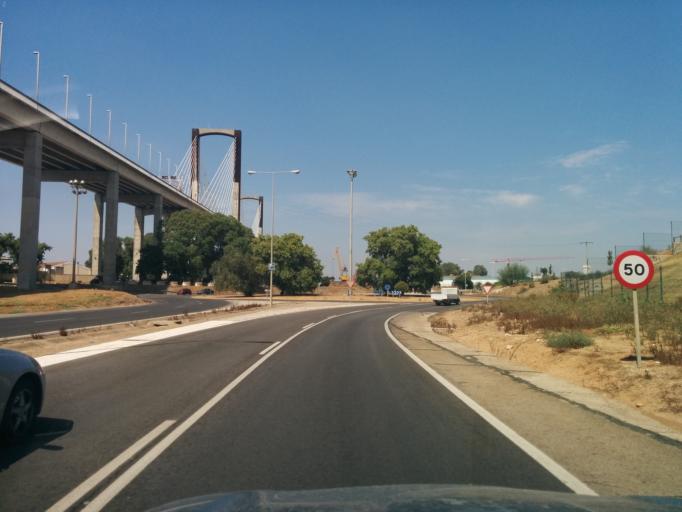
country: ES
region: Andalusia
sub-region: Provincia de Sevilla
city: Gelves
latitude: 37.3460
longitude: -5.9888
